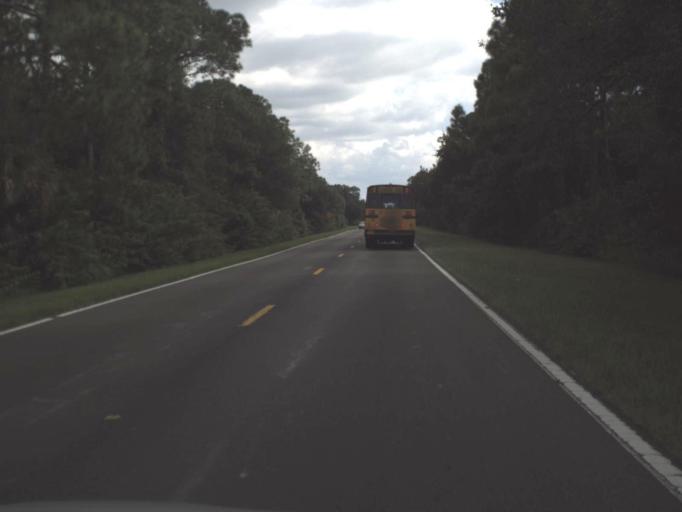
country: US
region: Florida
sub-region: Sarasota County
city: Warm Mineral Springs
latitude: 27.0550
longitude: -82.3110
